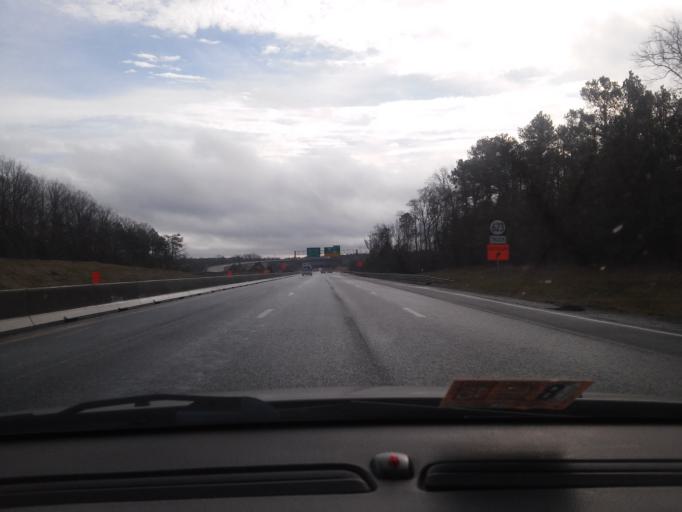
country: US
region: Virginia
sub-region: Henrico County
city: Wyndham
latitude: 37.6770
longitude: -77.6585
